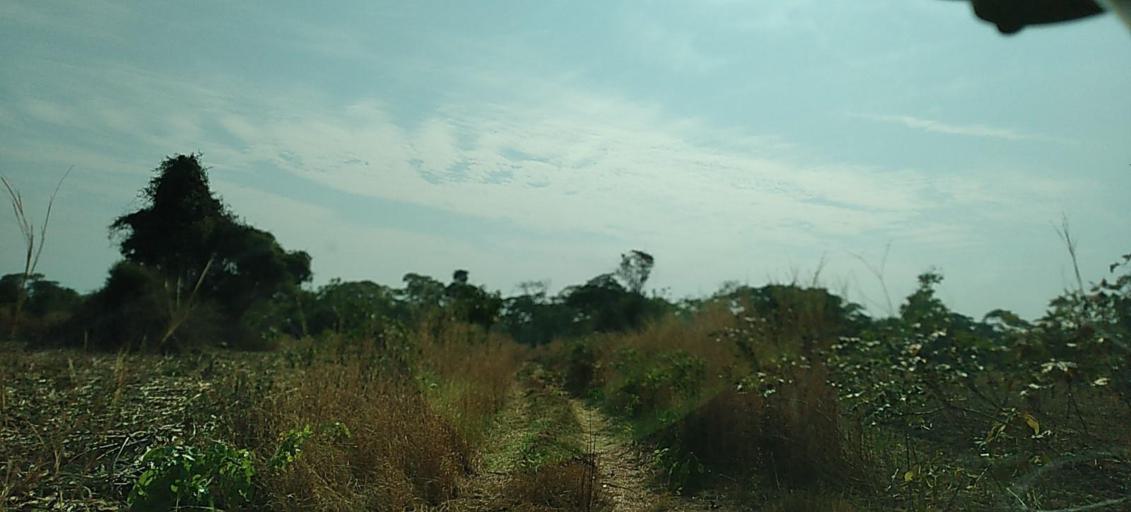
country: ZM
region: North-Western
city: Kalengwa
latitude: -13.2370
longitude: 25.0565
